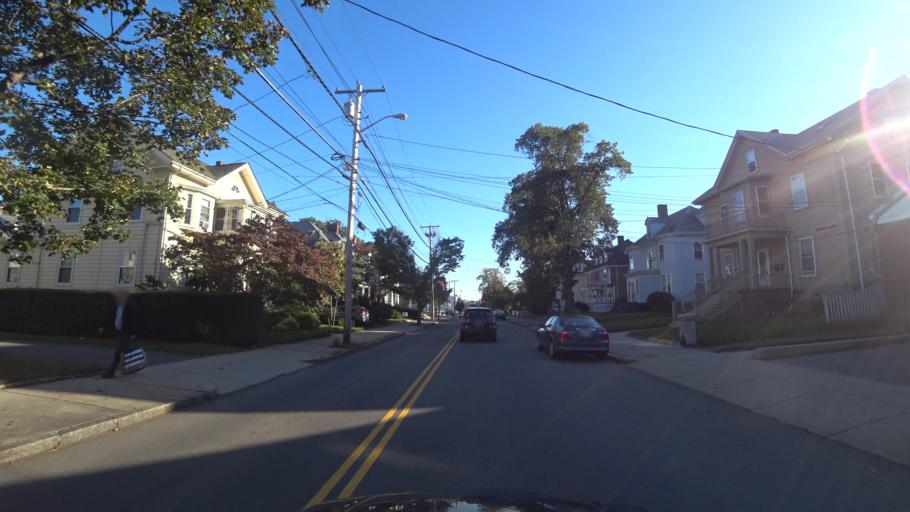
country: US
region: Massachusetts
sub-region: Middlesex County
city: Malden
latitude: 42.4280
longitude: -71.0813
